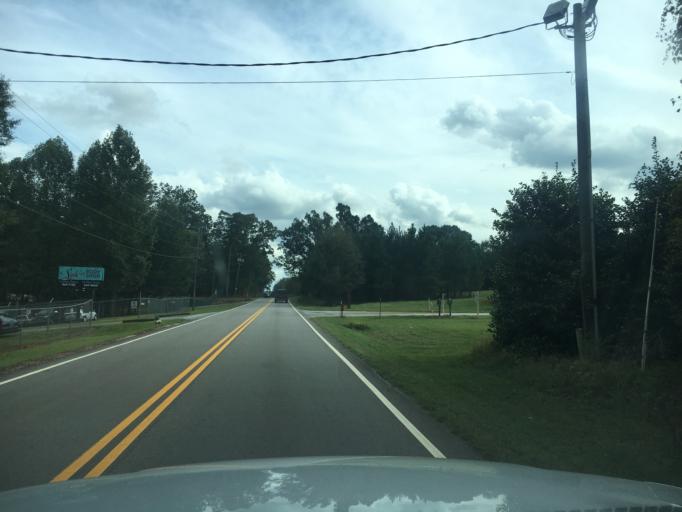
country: US
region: South Carolina
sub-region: Spartanburg County
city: Wellford
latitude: 34.9215
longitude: -82.0620
